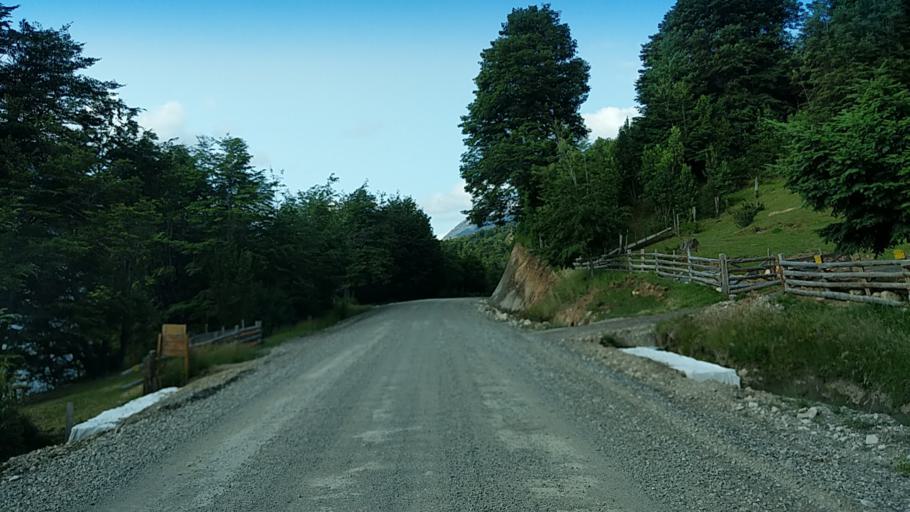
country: CL
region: Los Lagos
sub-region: Provincia de Palena
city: Futaleufu
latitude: -43.2426
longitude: -71.9298
